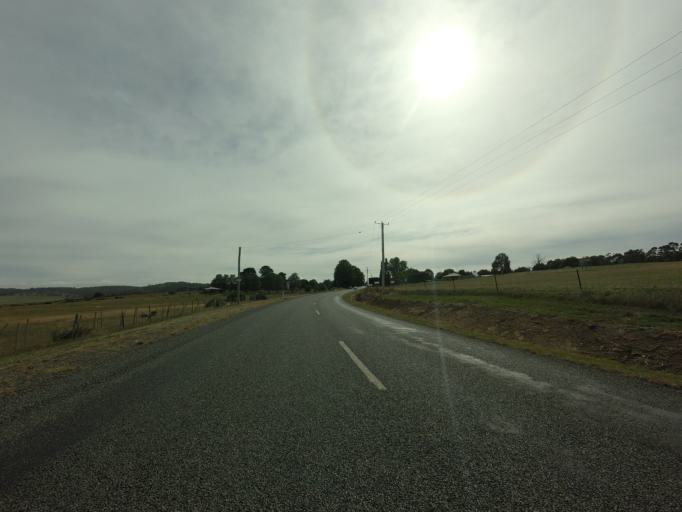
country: AU
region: Tasmania
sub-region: Brighton
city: Bridgewater
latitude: -42.3069
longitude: 147.3609
